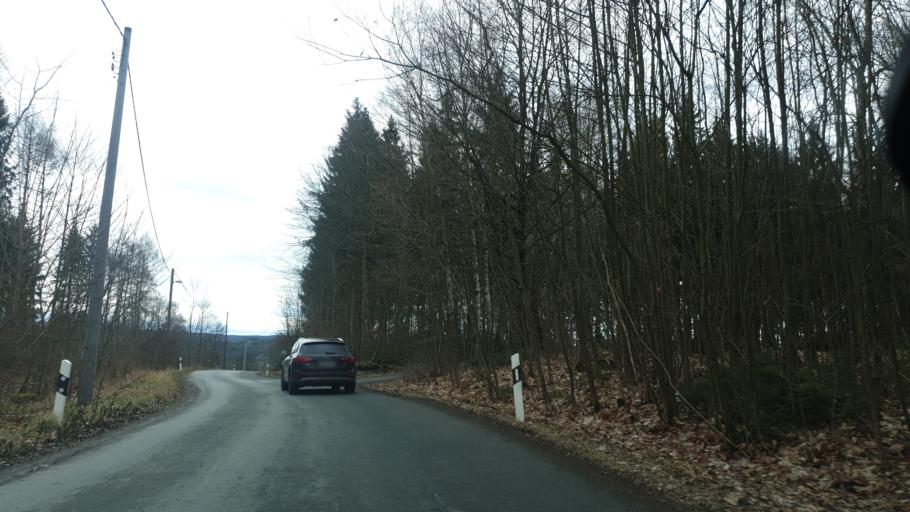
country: DE
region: Saxony
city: Bad Elster
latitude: 50.2743
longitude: 12.2730
